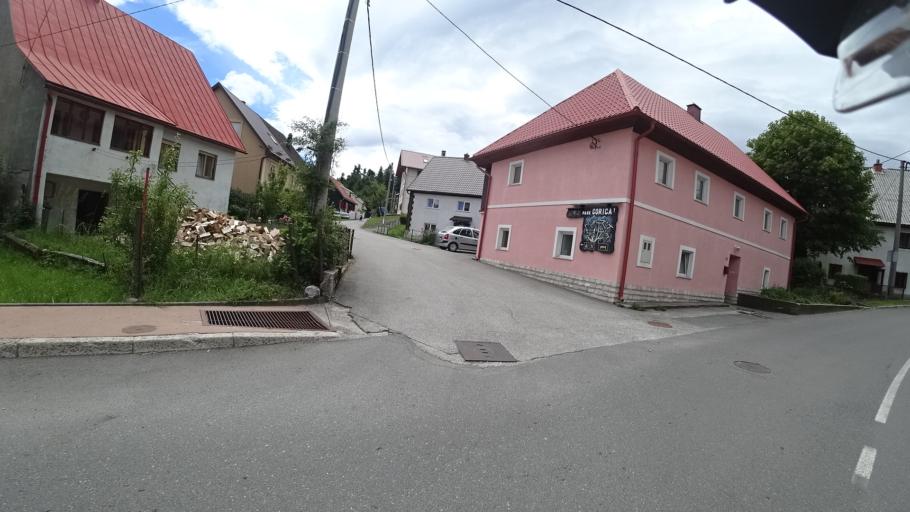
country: HR
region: Primorsko-Goranska
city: Hreljin
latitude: 45.3041
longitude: 14.7116
